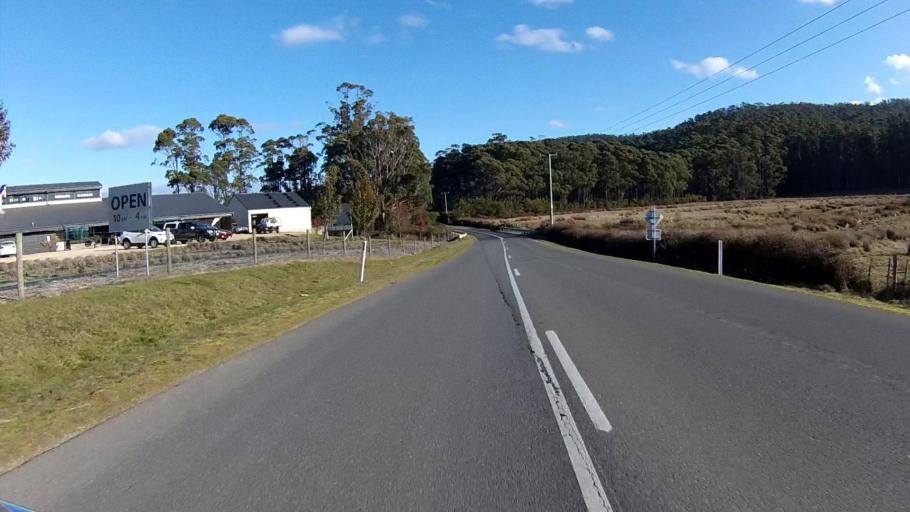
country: AU
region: Tasmania
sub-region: Clarence
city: Sandford
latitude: -43.1062
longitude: 147.8634
